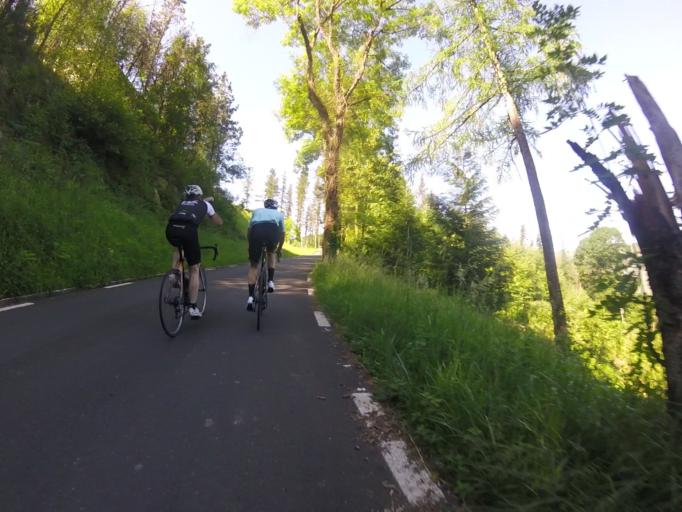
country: ES
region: Basque Country
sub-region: Provincia de Guipuzcoa
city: Beizama
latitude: 43.1352
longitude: -2.2250
